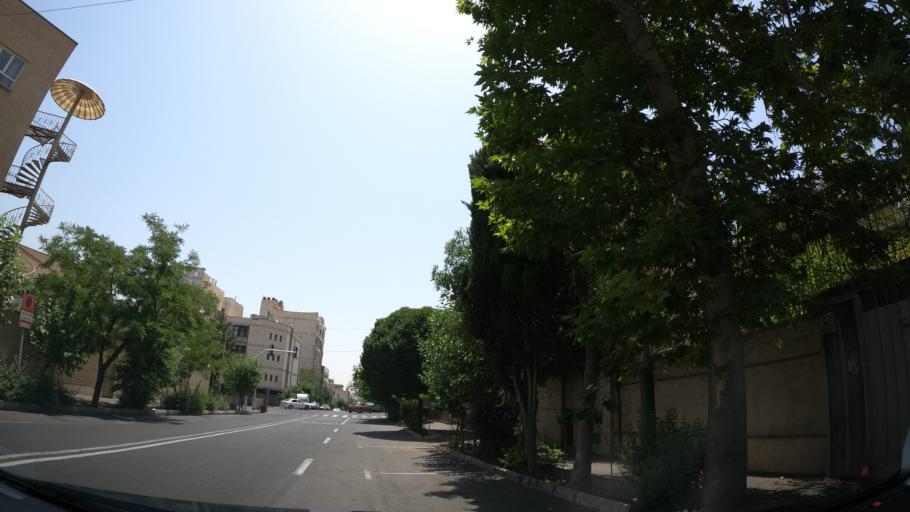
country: IR
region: Tehran
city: Tehran
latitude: 35.7206
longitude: 51.4261
